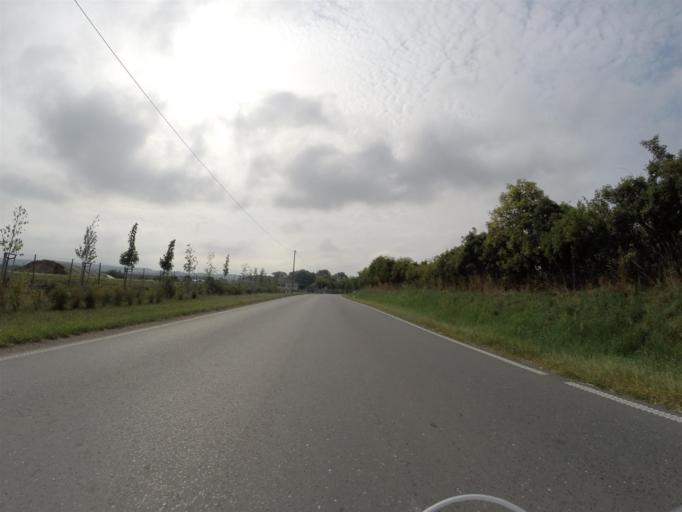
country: DE
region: Thuringia
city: Schongleina
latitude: 50.9218
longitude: 11.7309
